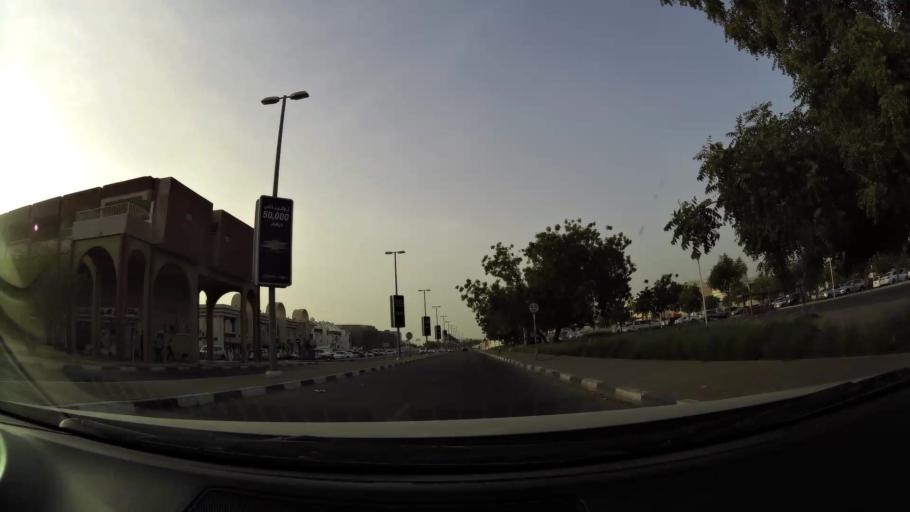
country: AE
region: Abu Dhabi
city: Al Ain
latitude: 24.2425
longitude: 55.7249
